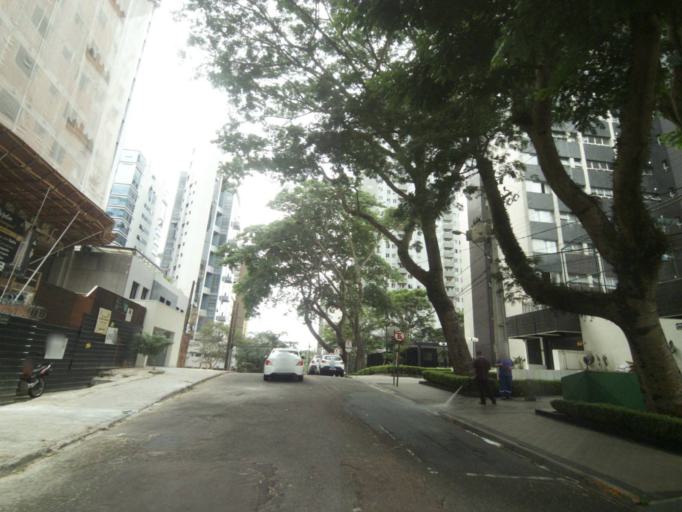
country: BR
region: Parana
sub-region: Curitiba
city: Curitiba
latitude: -25.4343
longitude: -49.3008
